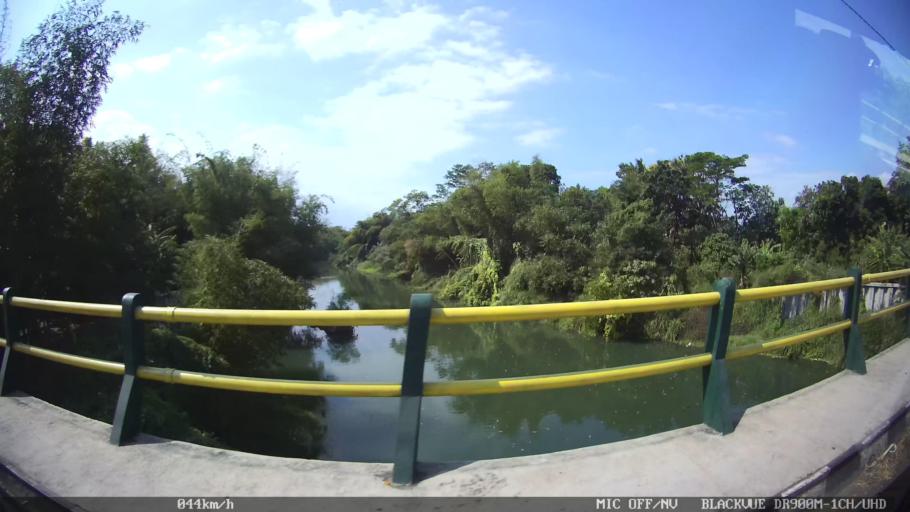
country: ID
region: Daerah Istimewa Yogyakarta
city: Sewon
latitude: -7.9154
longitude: 110.3751
